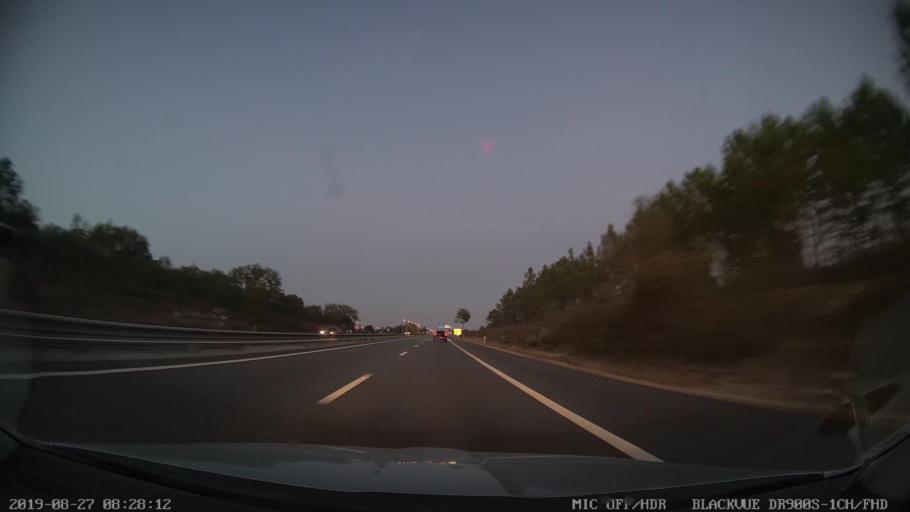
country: PT
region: Setubal
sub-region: Setubal
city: Setubal
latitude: 38.6011
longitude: -8.6827
